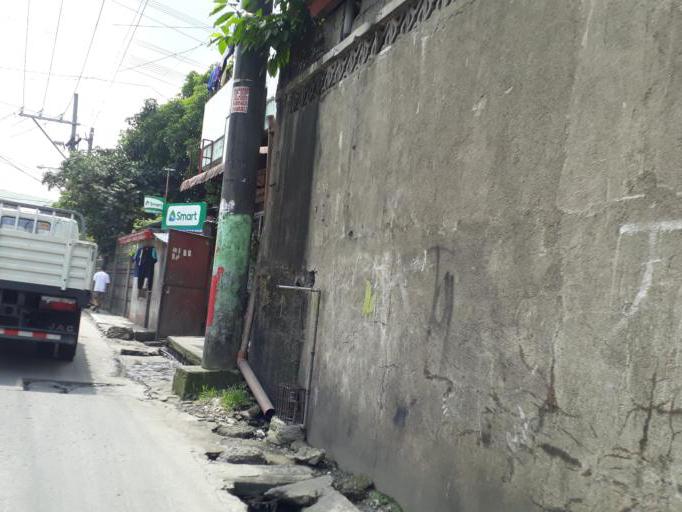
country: PH
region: Calabarzon
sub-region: Province of Rizal
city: Valenzuela
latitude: 14.7052
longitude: 121.0102
